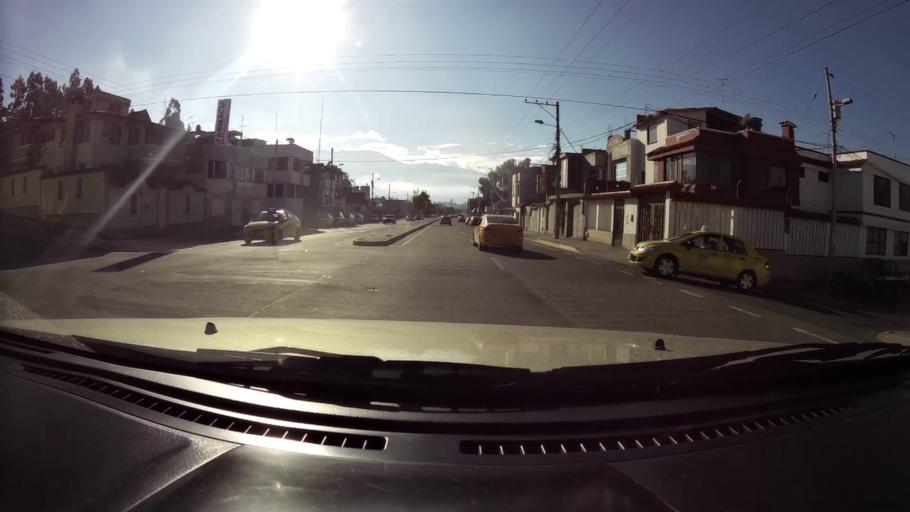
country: EC
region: Chimborazo
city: Riobamba
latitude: -1.6715
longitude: -78.6359
